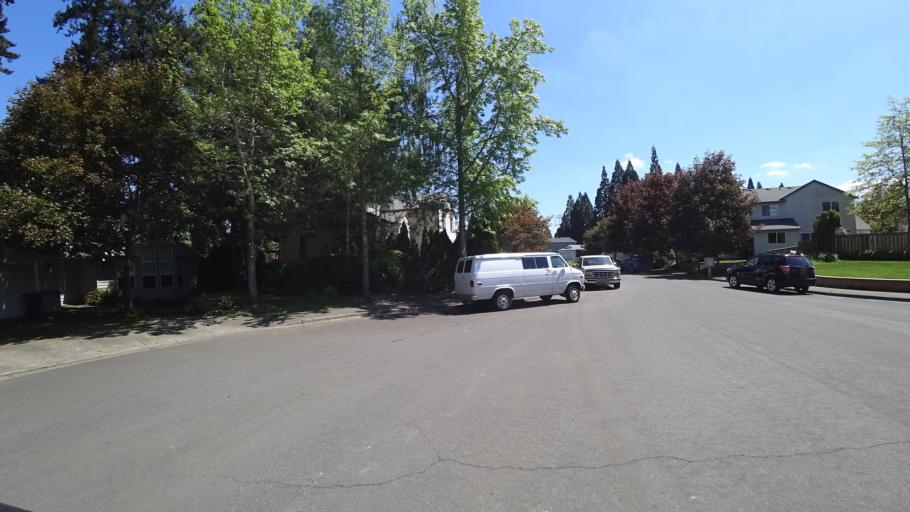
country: US
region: Oregon
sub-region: Washington County
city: Rockcreek
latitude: 45.5195
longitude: -122.8990
